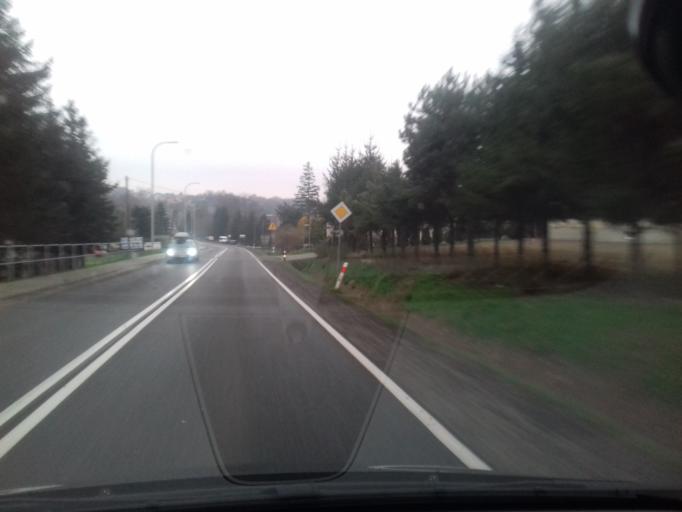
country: PL
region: Lesser Poland Voivodeship
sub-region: Powiat limanowski
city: Tymbark
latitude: 49.7217
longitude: 20.3401
